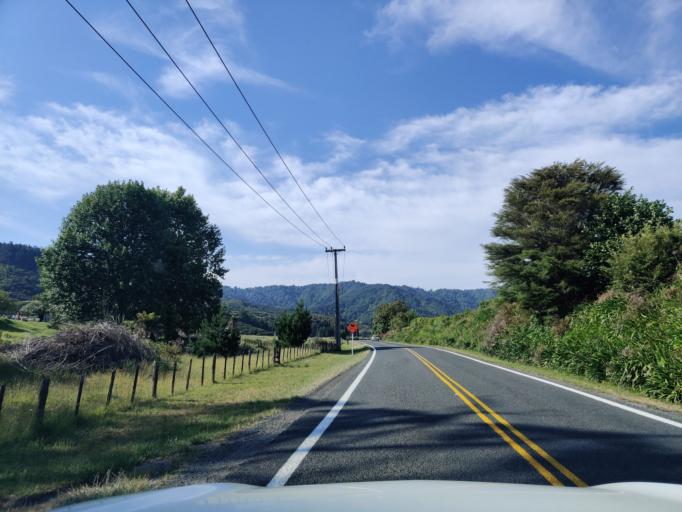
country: NZ
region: Waikato
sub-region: Waikato District
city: Ngaruawahia
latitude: -37.6484
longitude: 175.1454
